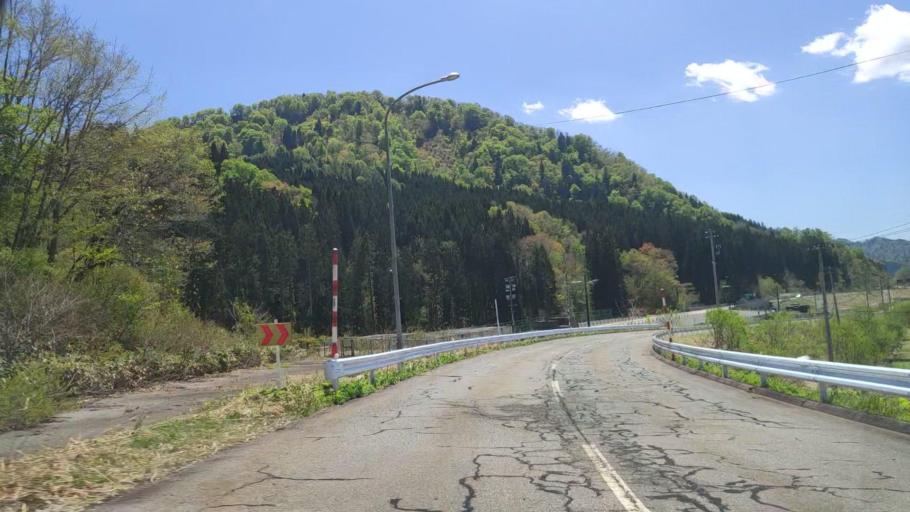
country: JP
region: Yamagata
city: Shinjo
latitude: 38.9539
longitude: 140.3589
